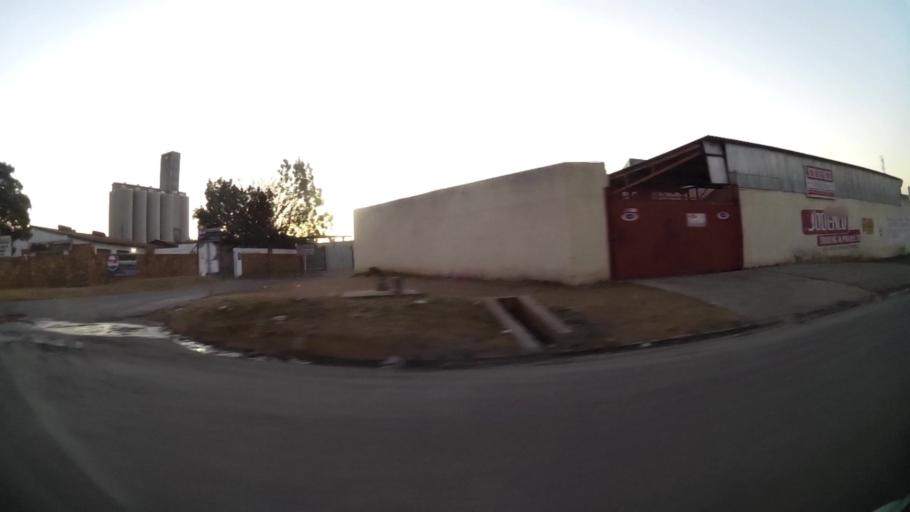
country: ZA
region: North-West
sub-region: Bojanala Platinum District Municipality
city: Rustenburg
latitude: -25.6765
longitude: 27.2591
